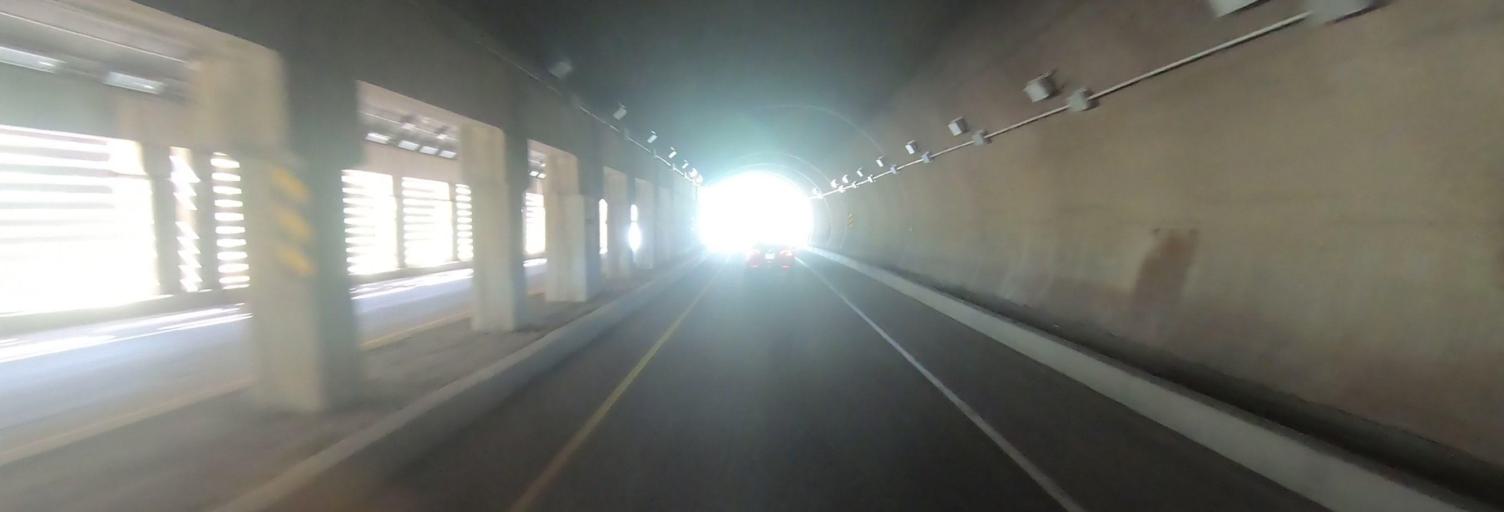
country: CA
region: British Columbia
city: Golden
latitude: 51.3272
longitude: -117.4710
